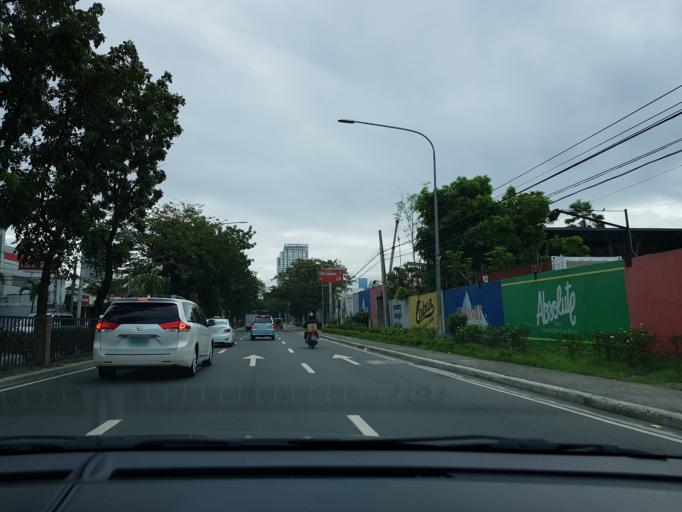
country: PH
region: Metro Manila
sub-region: San Juan
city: San Juan
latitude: 14.6061
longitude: 121.0411
